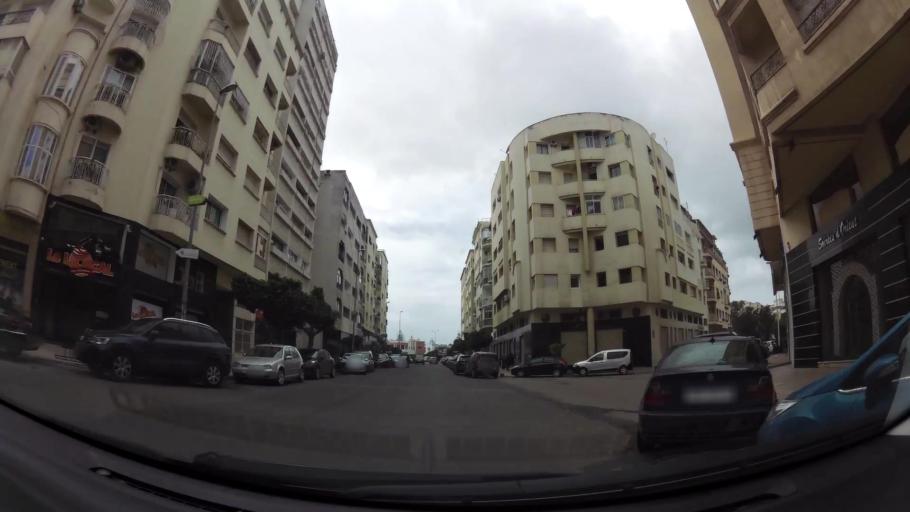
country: MA
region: Grand Casablanca
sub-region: Casablanca
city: Casablanca
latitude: 33.5944
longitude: -7.6432
